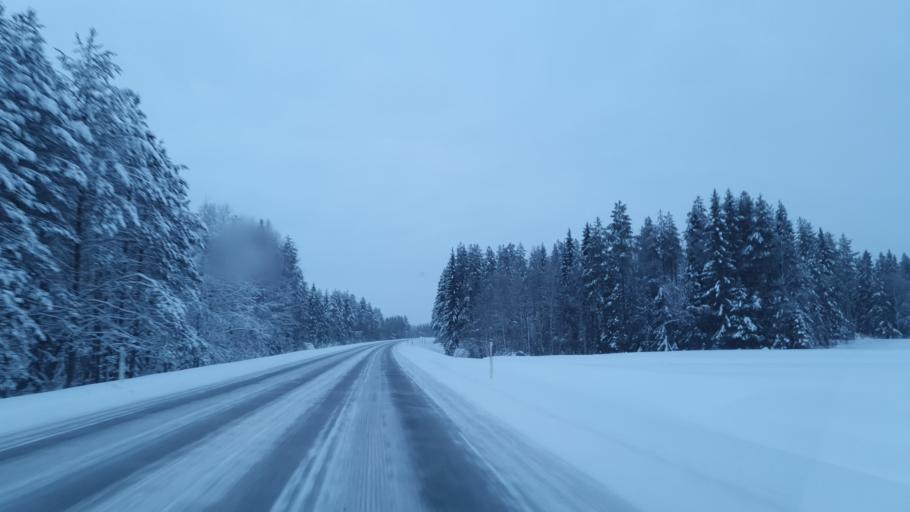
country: FI
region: Kainuu
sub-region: Kajaani
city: Vaala
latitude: 64.5984
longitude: 26.6831
